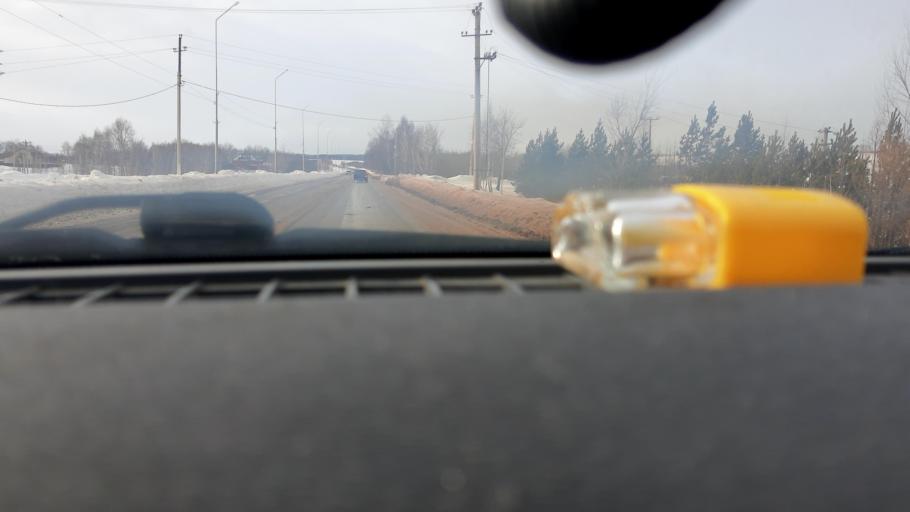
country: RU
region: Bashkortostan
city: Davlekanovo
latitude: 54.2153
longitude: 54.9993
